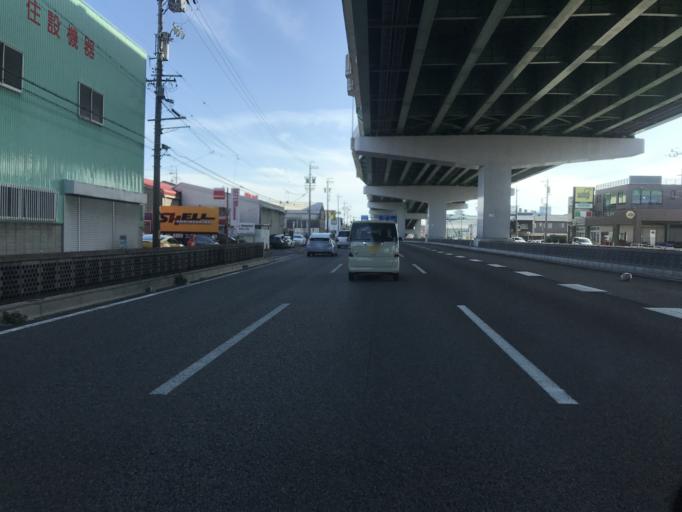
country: JP
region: Aichi
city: Iwakura
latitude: 35.2347
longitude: 136.8497
